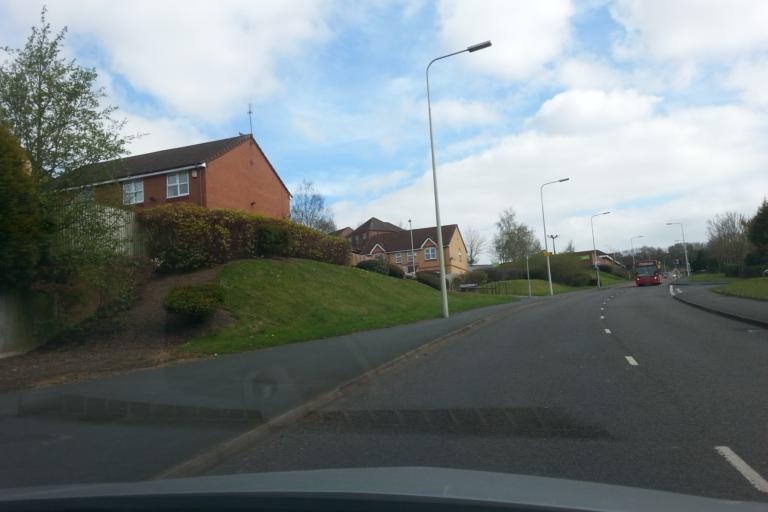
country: GB
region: England
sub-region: Dudley
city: Brierley Hill
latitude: 52.5172
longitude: -2.1171
